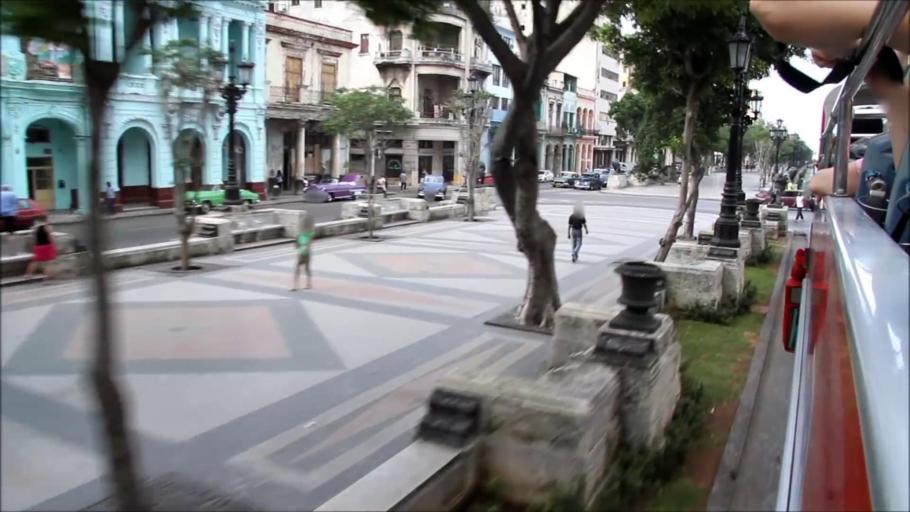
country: CU
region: La Habana
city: Centro Habana
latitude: 23.1411
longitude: -82.3587
